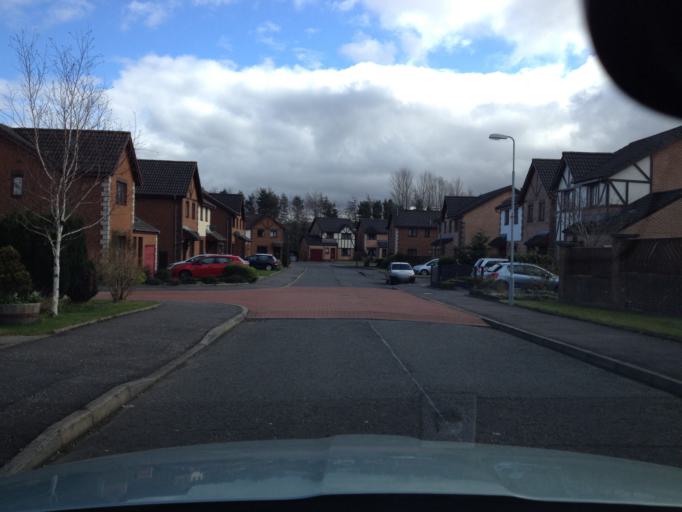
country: GB
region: Scotland
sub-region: West Lothian
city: Livingston
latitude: 55.8724
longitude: -3.5181
